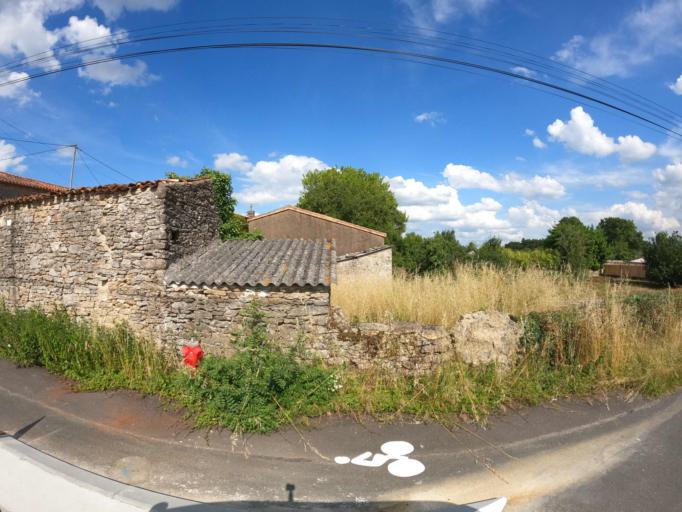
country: FR
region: Pays de la Loire
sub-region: Departement de la Loire-Atlantique
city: Remouille
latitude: 47.0763
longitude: -1.3662
